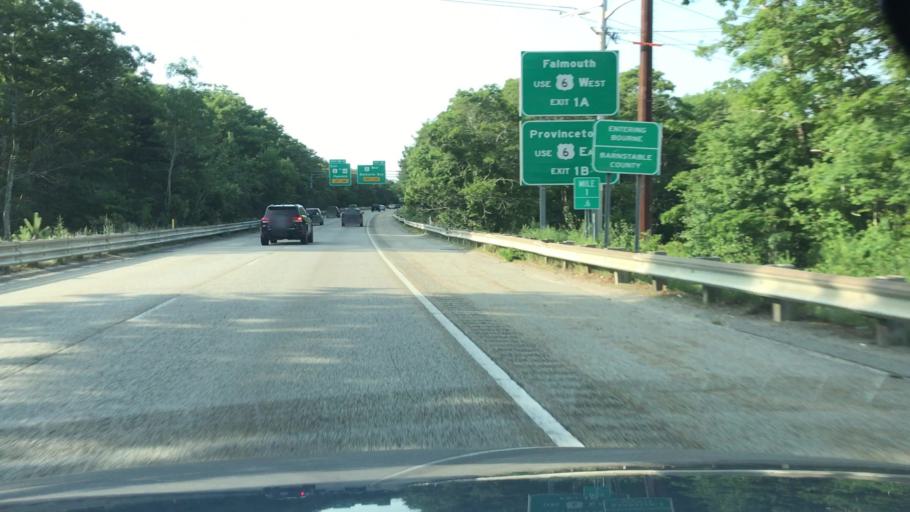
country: US
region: Massachusetts
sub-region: Barnstable County
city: Sagamore
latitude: 41.8022
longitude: -70.5477
